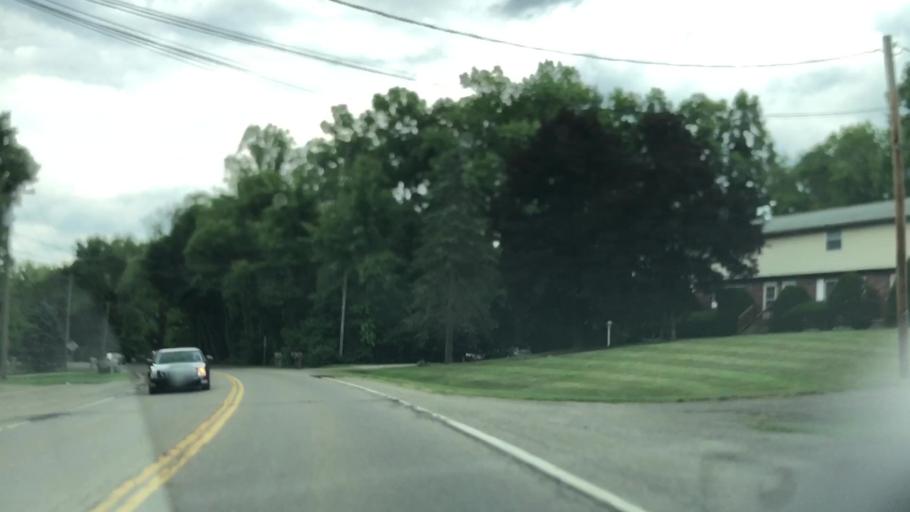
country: US
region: Ohio
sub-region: Summit County
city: New Franklin
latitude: 40.9699
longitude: -81.5207
